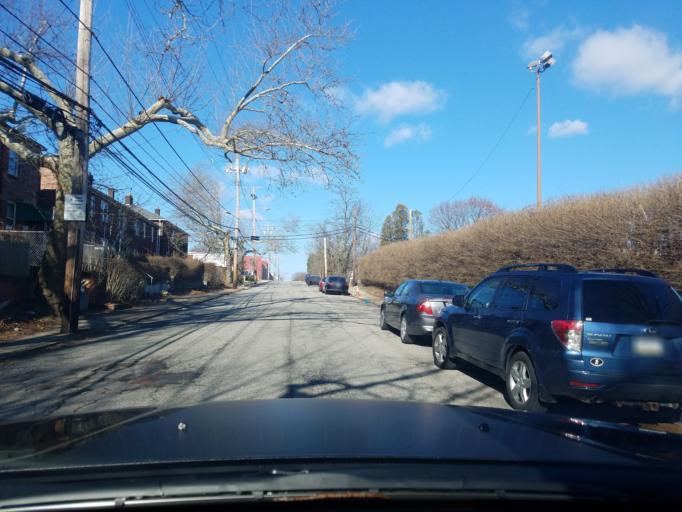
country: US
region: Pennsylvania
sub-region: Allegheny County
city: Wilkinsburg
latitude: 40.4488
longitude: -79.8968
